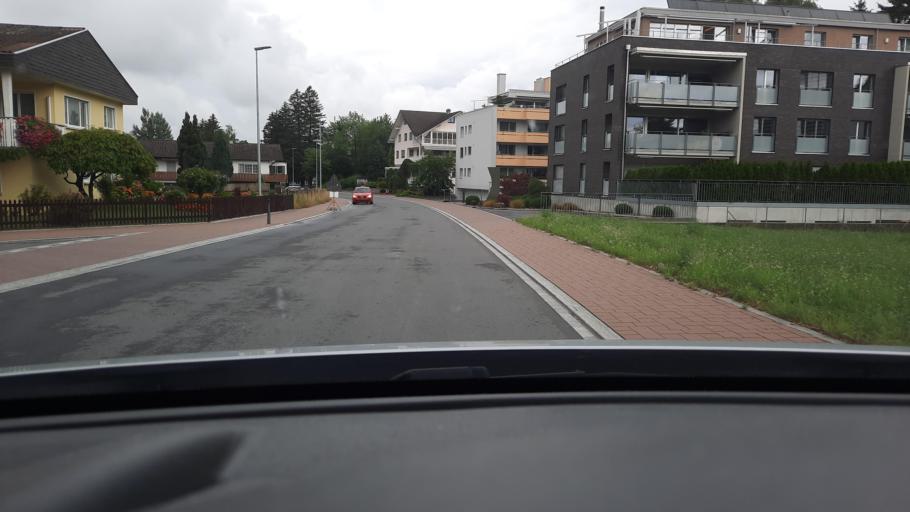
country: LI
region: Schaan
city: Schaan
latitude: 47.1561
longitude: 9.5065
